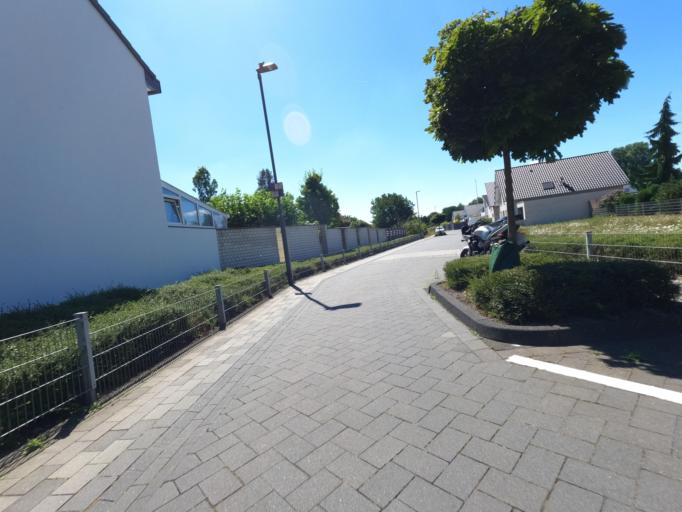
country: DE
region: North Rhine-Westphalia
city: Baesweiler
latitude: 50.8945
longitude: 6.1827
